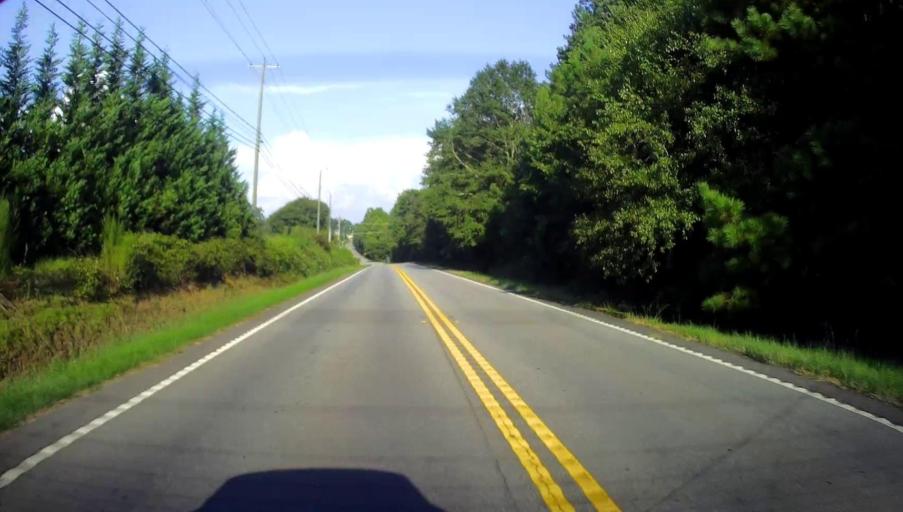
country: US
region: Georgia
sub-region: Houston County
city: Perry
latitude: 32.5061
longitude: -83.6475
